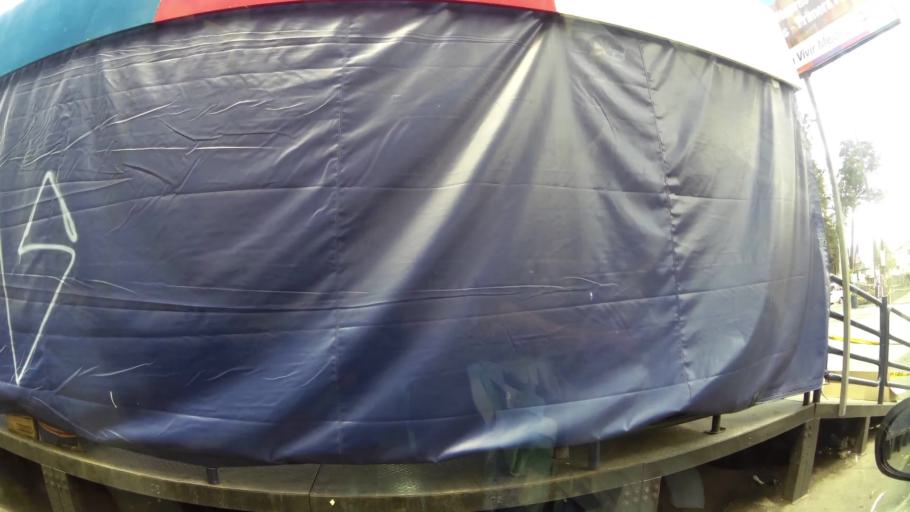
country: EC
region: Pichincha
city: Quito
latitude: -0.2005
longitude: -78.4970
